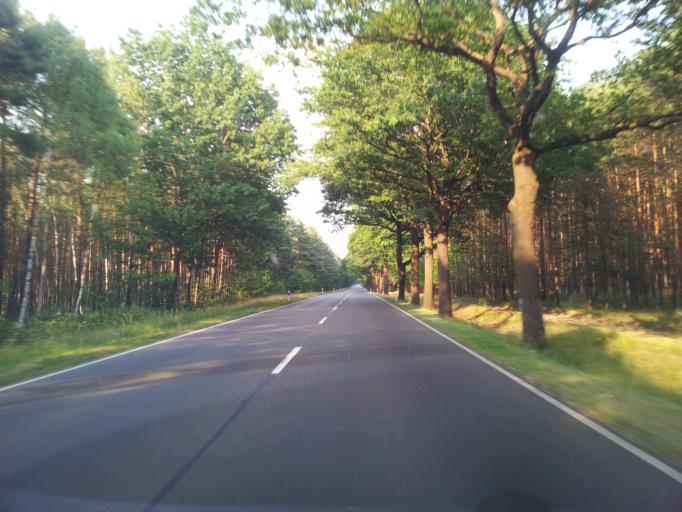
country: DE
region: Saxony
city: Ossling
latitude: 51.4121
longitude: 14.1569
